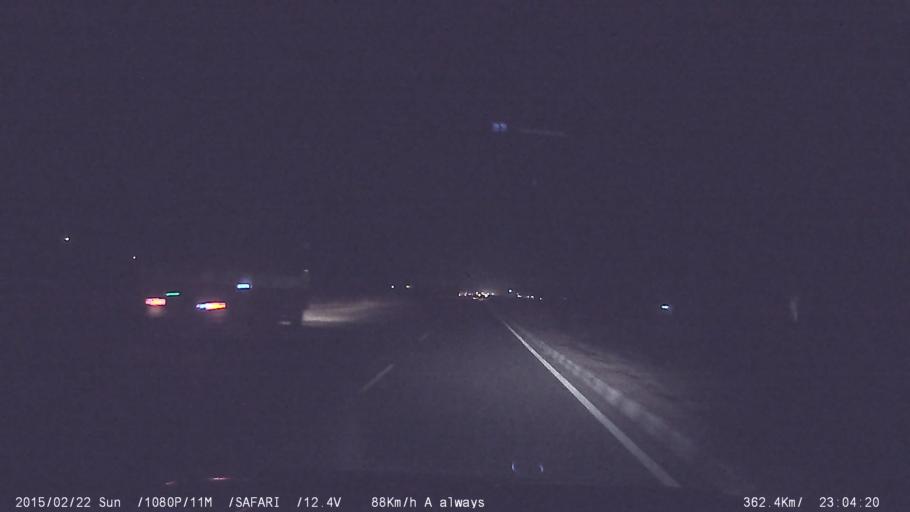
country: IN
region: Tamil Nadu
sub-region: Namakkal
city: Rasipuram
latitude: 11.4010
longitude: 78.1598
